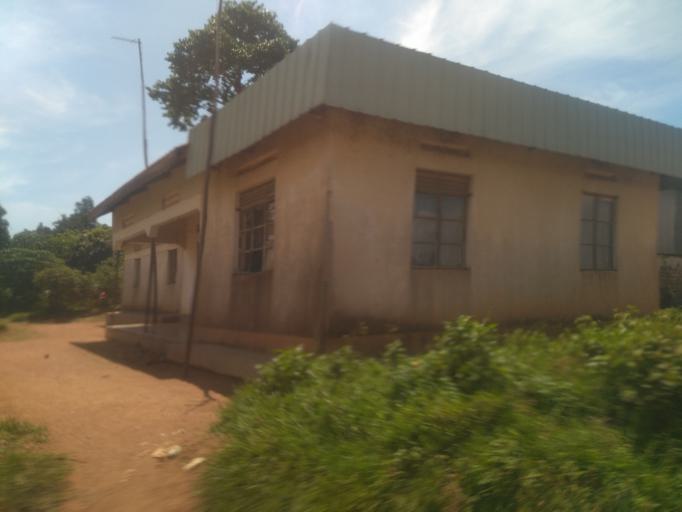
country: UG
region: Central Region
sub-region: Wakiso District
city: Entebbe
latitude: 0.0358
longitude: 32.4324
